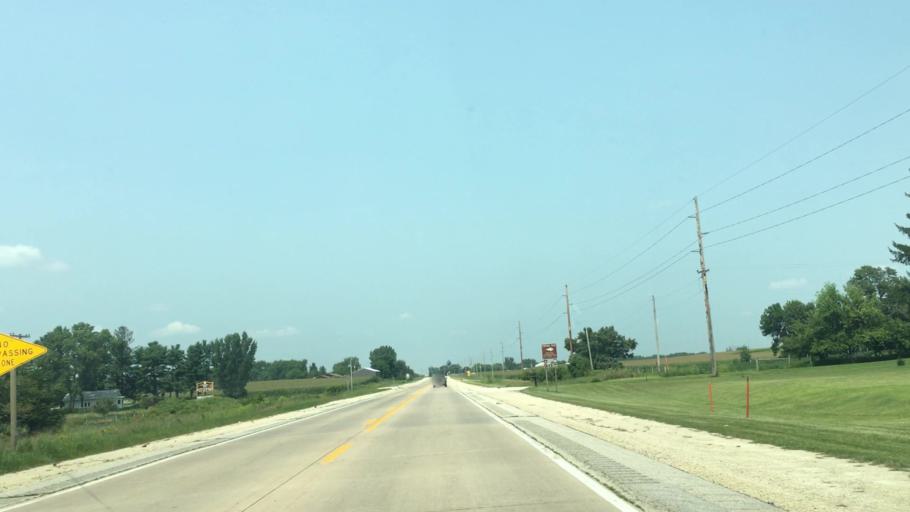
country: US
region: Iowa
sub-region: Fayette County
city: Oelwein
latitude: 42.6023
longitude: -91.9025
